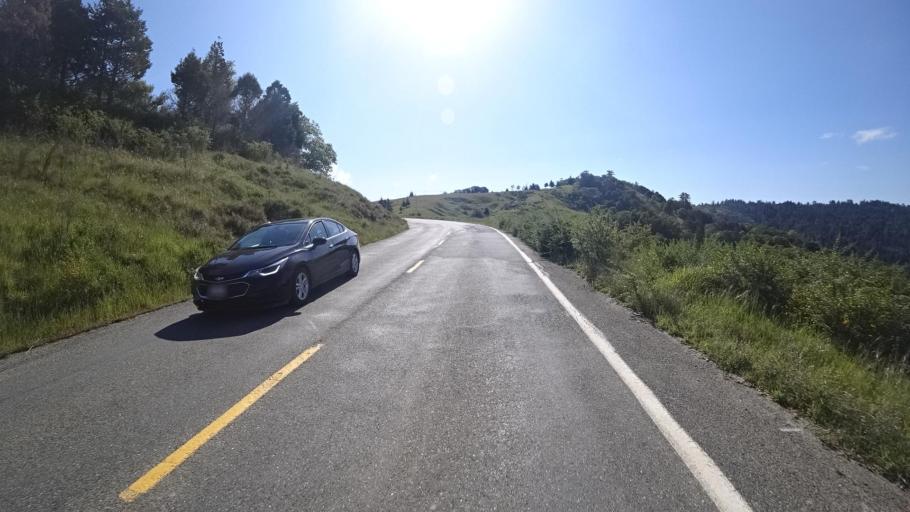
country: US
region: California
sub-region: Humboldt County
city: Redway
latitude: 40.1140
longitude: -123.7593
